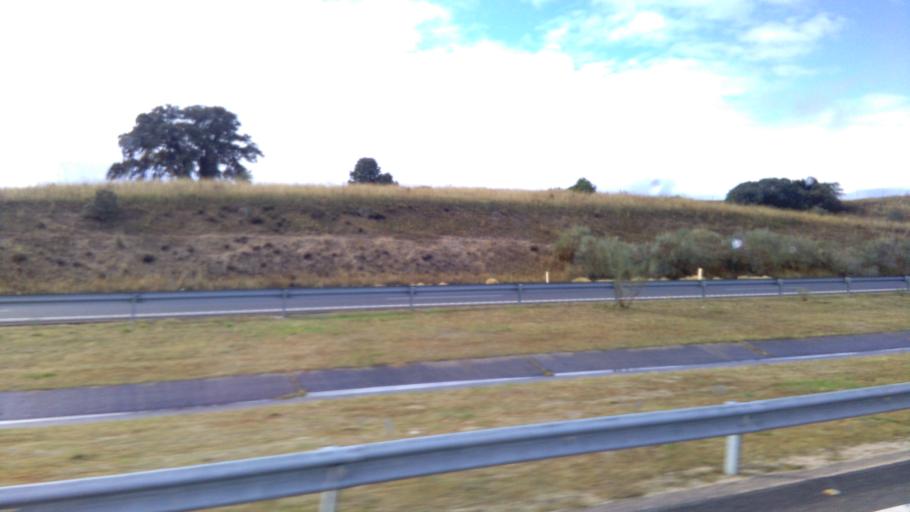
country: ES
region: Madrid
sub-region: Provincia de Madrid
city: El Alamo
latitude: 40.2621
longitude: -3.9940
